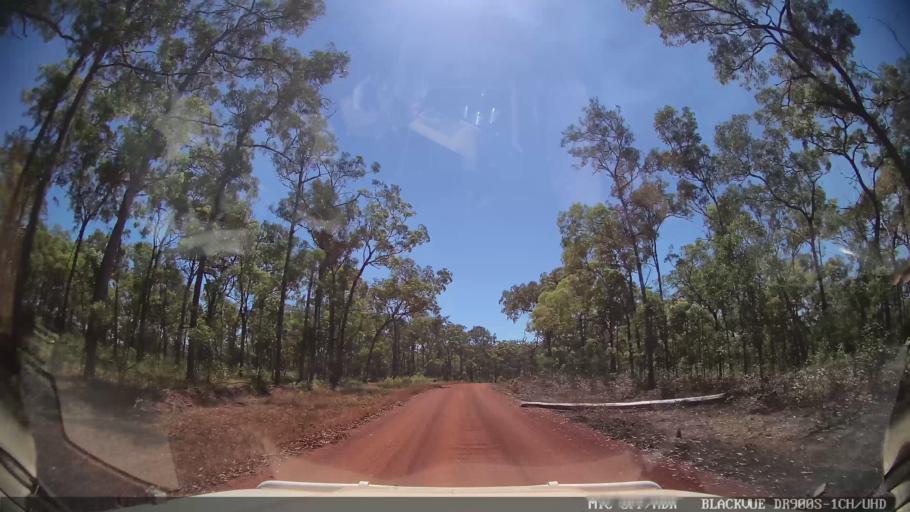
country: AU
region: Queensland
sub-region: Torres
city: Thursday Island
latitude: -10.9727
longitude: 142.3406
